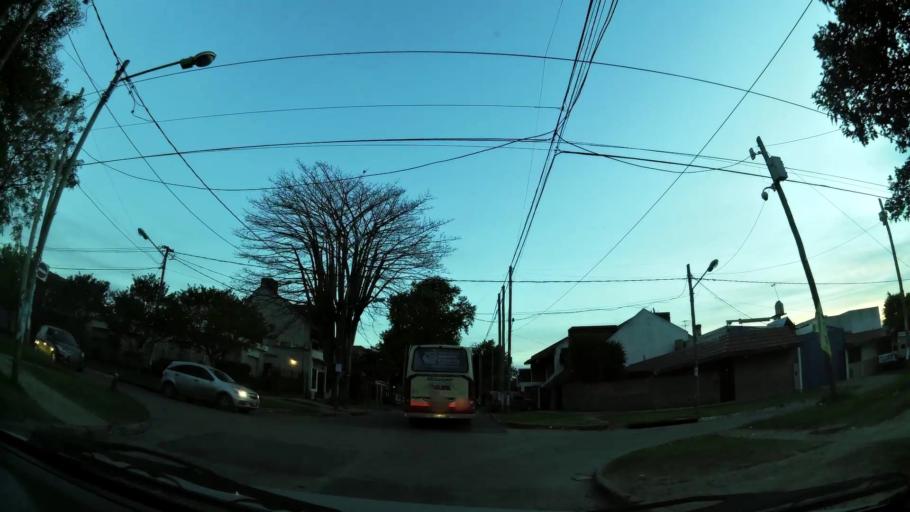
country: AR
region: Buenos Aires
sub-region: Partido de Quilmes
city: Quilmes
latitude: -34.8041
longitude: -58.2835
